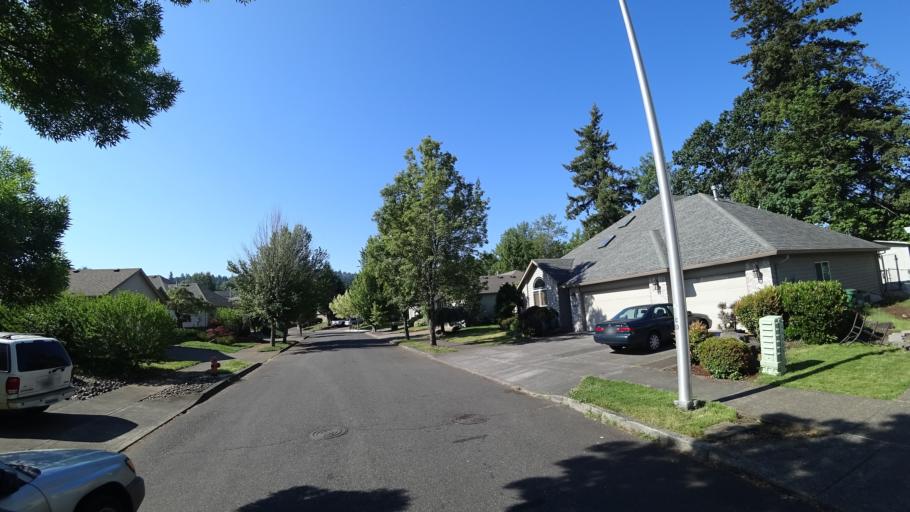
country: US
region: Oregon
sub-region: Multnomah County
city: Lents
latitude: 45.4706
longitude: -122.5528
